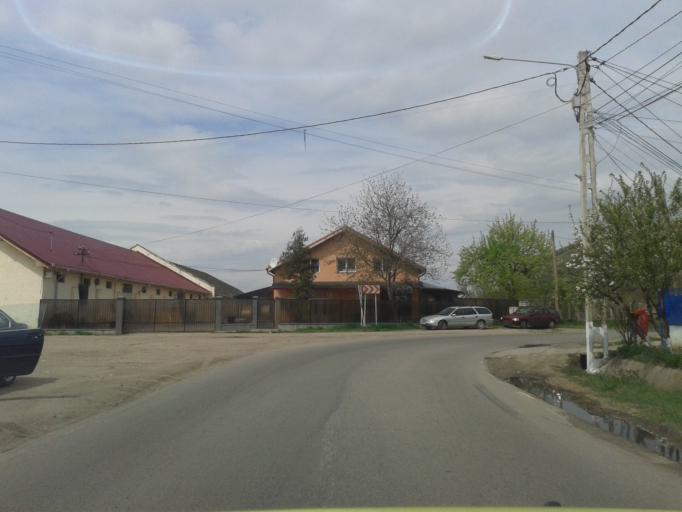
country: RO
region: Alba
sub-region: Comuna Valea Lunga
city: Valea Lunga
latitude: 46.1192
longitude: 24.0355
